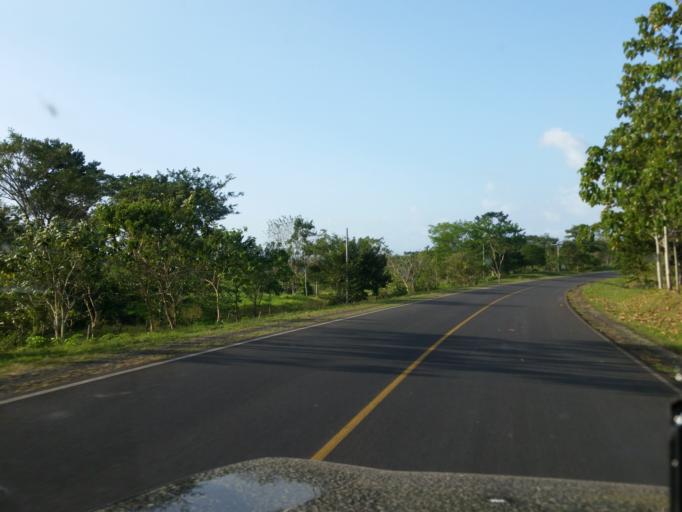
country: NI
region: Rio San Juan
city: San Carlos
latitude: 11.2108
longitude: -84.6868
